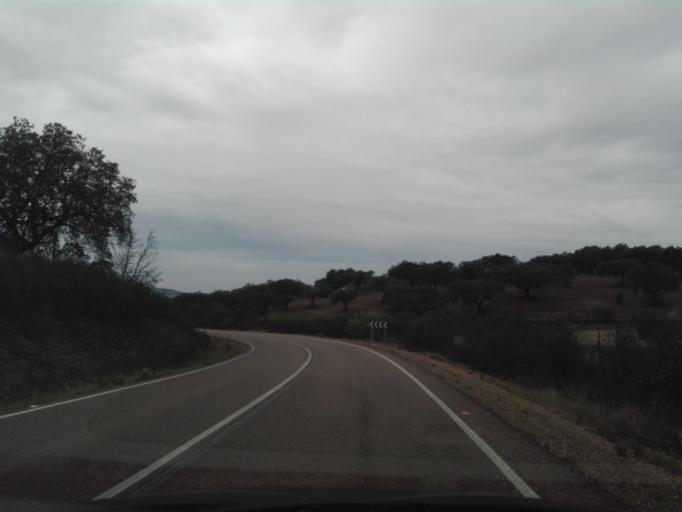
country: ES
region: Extremadura
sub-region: Provincia de Badajoz
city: Alburquerque
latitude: 39.1983
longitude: -7.0044
